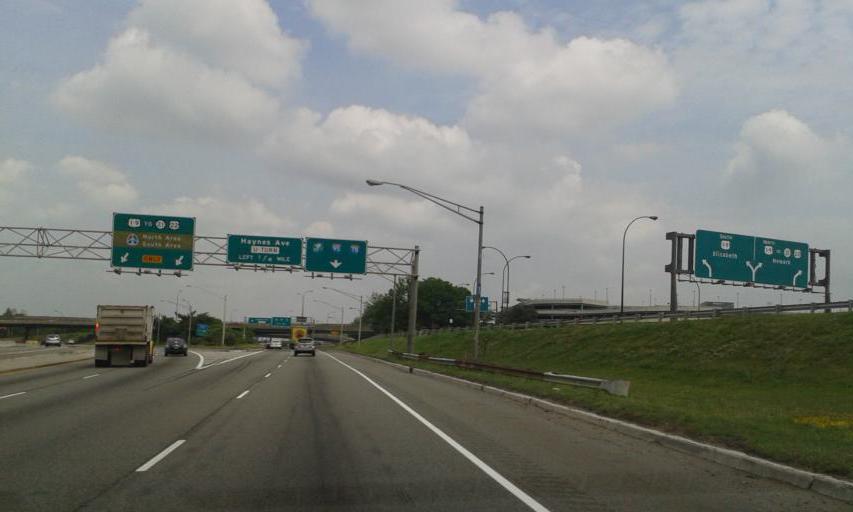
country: US
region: New Jersey
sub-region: Union County
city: Elizabeth
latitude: 40.6942
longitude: -74.1870
